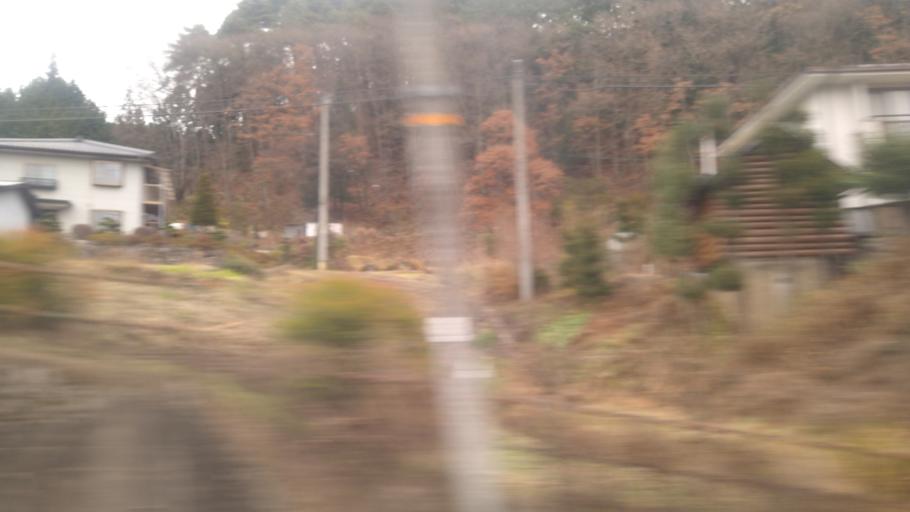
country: JP
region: Nagano
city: Ina
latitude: 35.8211
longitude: 137.6827
